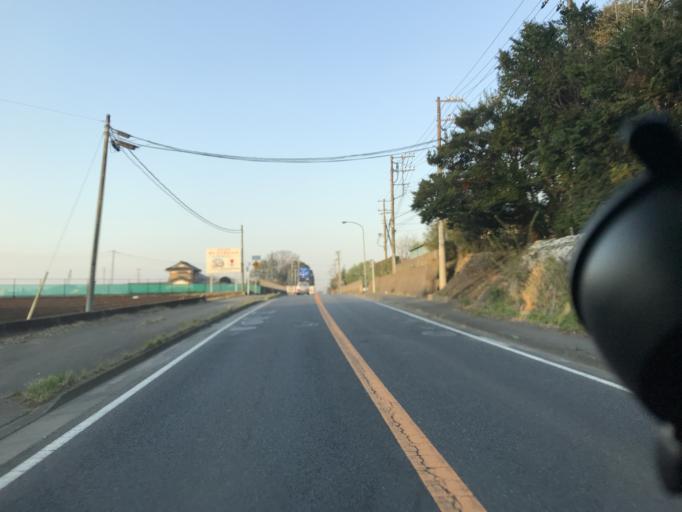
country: JP
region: Chiba
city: Narita
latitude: 35.8106
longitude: 140.3866
